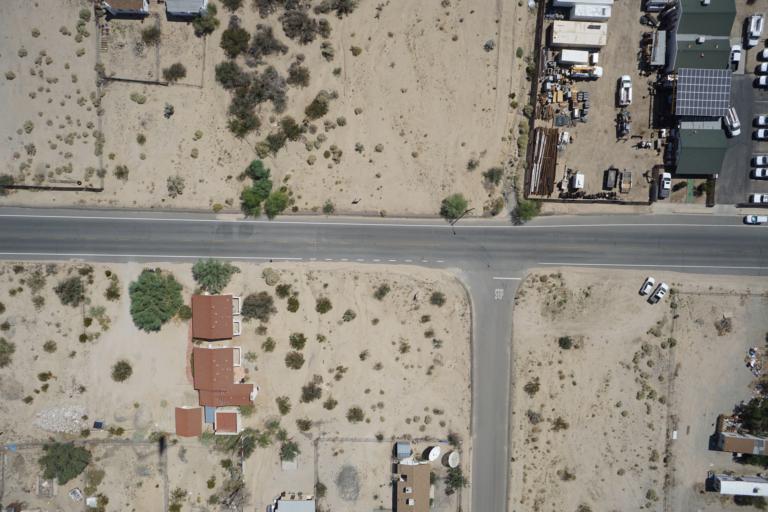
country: US
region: California
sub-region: San Bernardino County
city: Twentynine Palms
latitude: 34.1323
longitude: -116.0544
